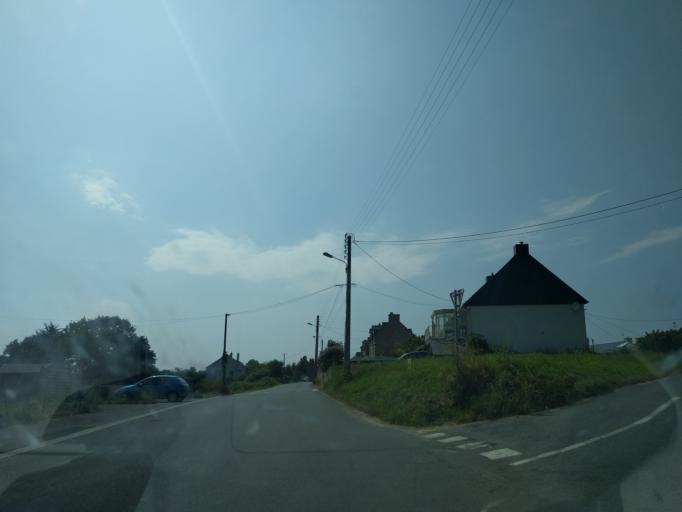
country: FR
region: Brittany
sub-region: Departement des Cotes-d'Armor
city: Plurien
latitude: 48.6385
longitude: -2.4280
